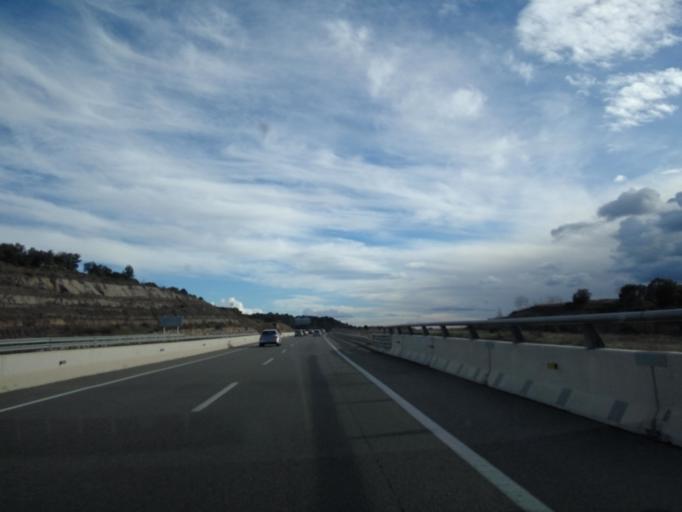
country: ES
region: Catalonia
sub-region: Provincia de Barcelona
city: Puig-reig
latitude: 41.9800
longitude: 1.8865
